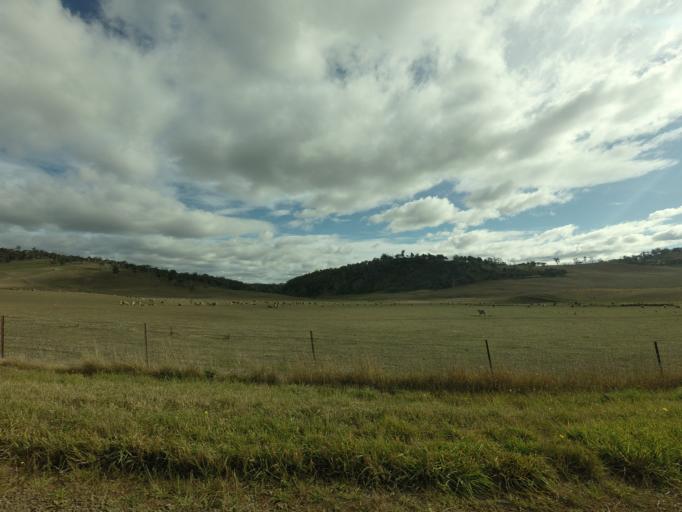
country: AU
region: Tasmania
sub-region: Brighton
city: Bridgewater
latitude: -42.4665
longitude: 147.2792
